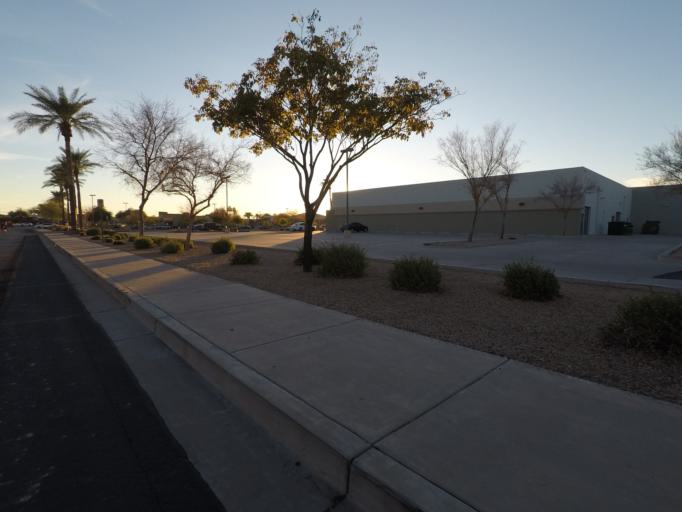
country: US
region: Arizona
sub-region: Maricopa County
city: Guadalupe
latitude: 33.3509
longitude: -111.9581
